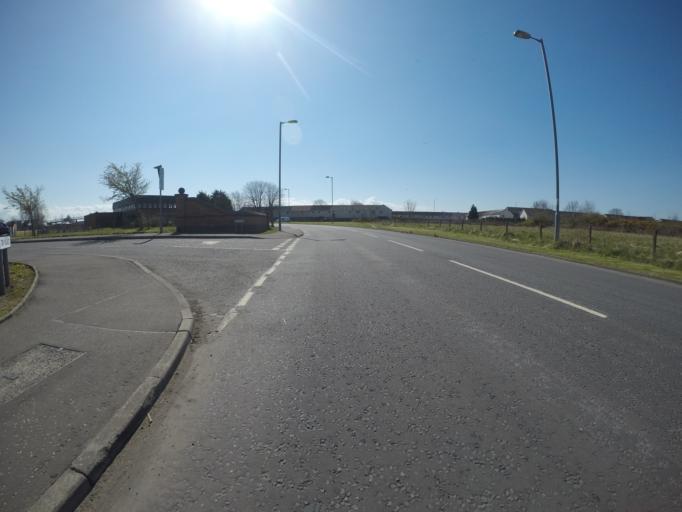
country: GB
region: Scotland
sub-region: North Ayrshire
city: Irvine
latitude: 55.6305
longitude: -4.6677
